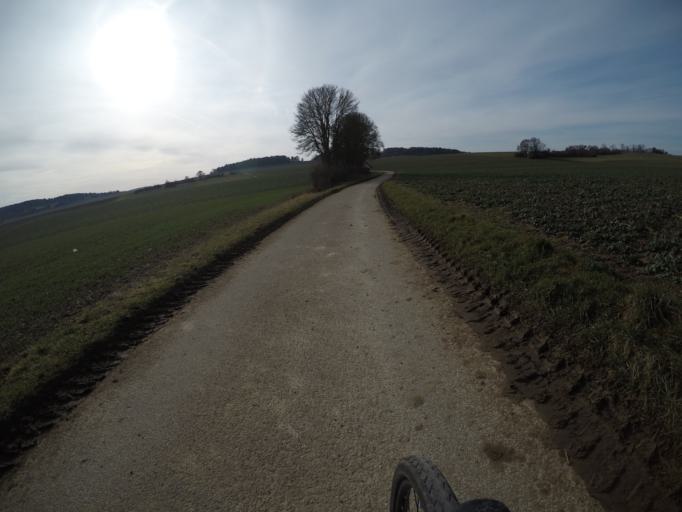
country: DE
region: Baden-Wuerttemberg
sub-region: Karlsruhe Region
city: Ostelsheim
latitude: 48.7048
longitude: 8.8657
